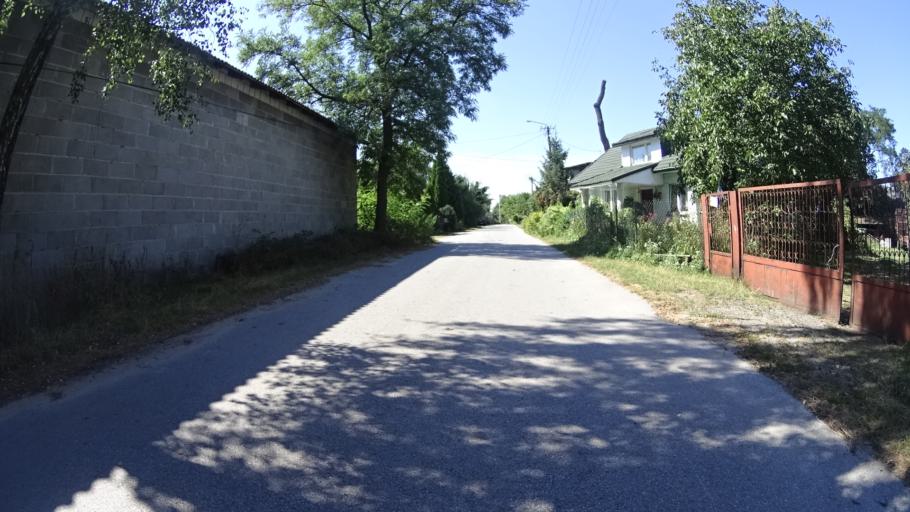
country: PL
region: Masovian Voivodeship
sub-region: Powiat bialobrzeski
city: Bialobrzegi
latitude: 51.6695
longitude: 20.9124
